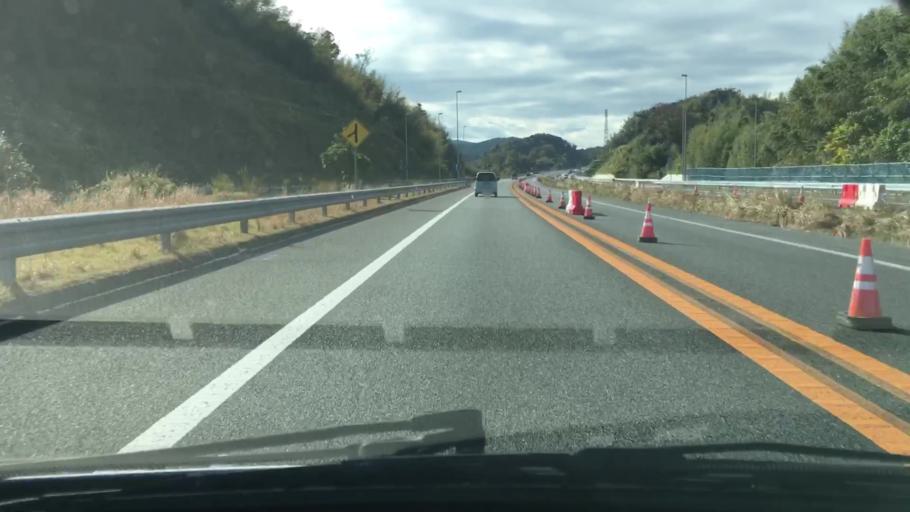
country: JP
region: Chiba
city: Kimitsu
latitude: 35.2826
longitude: 139.9263
